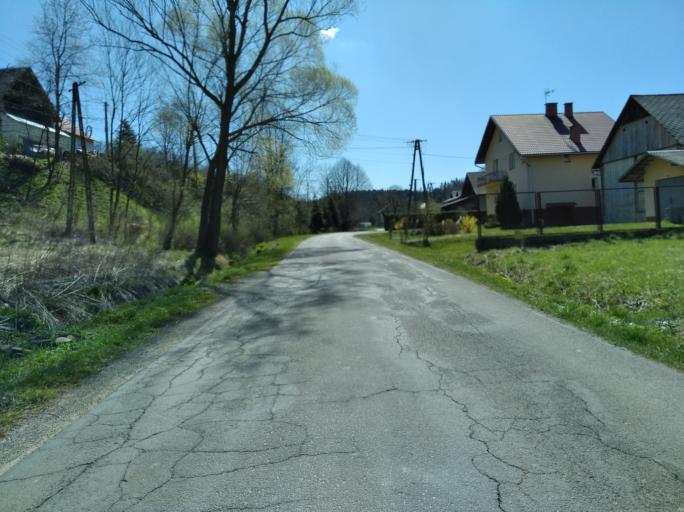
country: PL
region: Subcarpathian Voivodeship
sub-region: Powiat brzozowski
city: Jablonka
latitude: 49.7317
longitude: 22.1477
